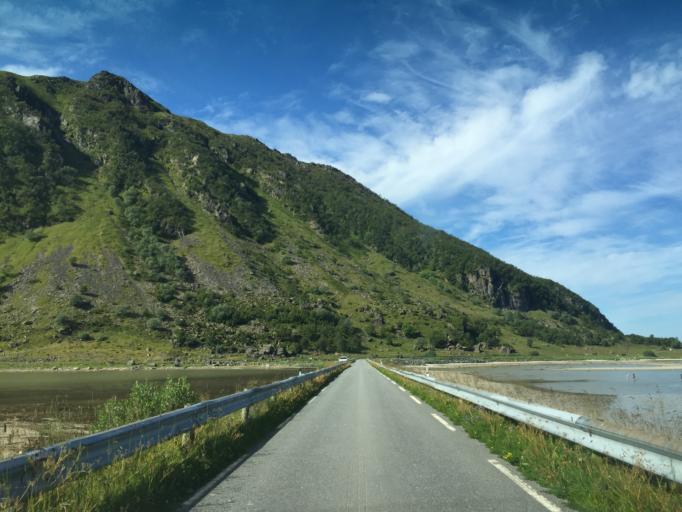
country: NO
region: Nordland
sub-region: Vagan
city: Svolvaer
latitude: 68.3953
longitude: 14.5444
